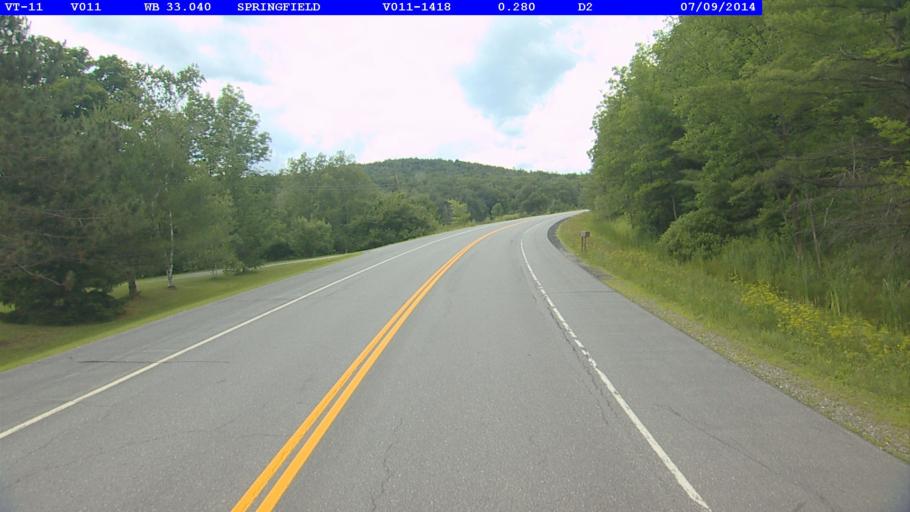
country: US
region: Vermont
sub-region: Windsor County
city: Chester
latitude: 43.2779
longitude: -72.5433
